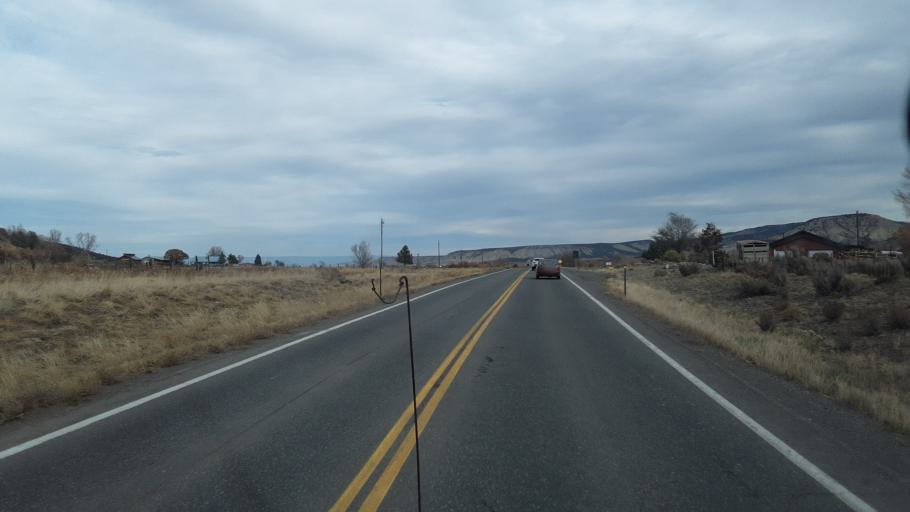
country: US
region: Colorado
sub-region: Montrose County
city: Montrose
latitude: 38.3016
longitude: -107.7734
